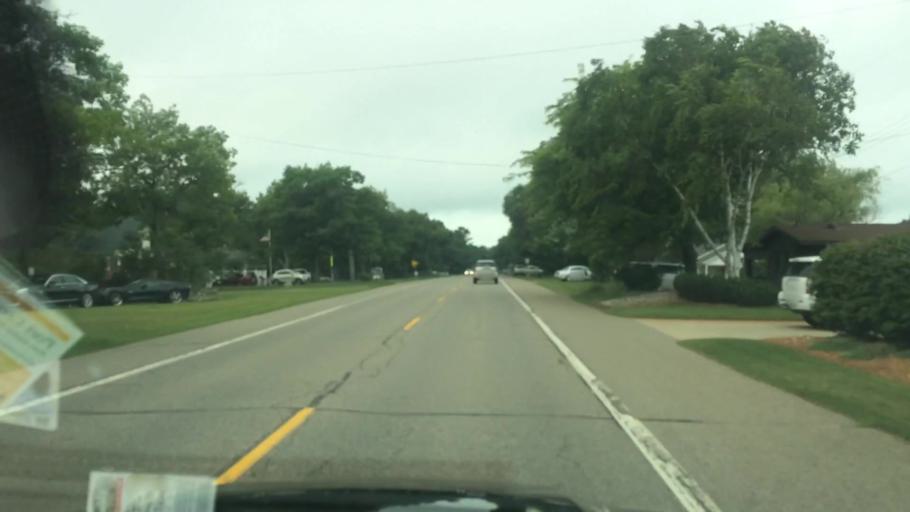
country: US
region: Michigan
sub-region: Huron County
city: Pigeon
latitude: 43.9768
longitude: -83.2417
